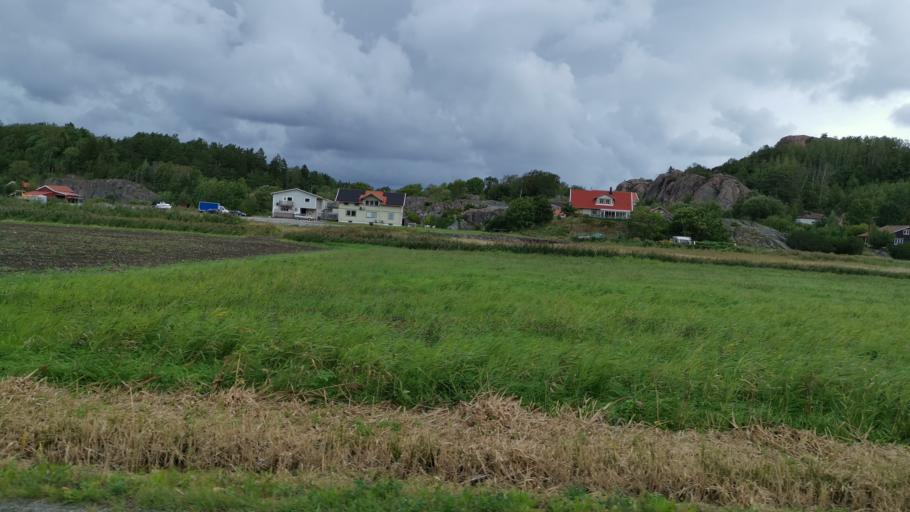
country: SE
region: Vaestra Goetaland
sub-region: Tjorns Kommun
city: Skaerhamn
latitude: 58.0404
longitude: 11.6067
